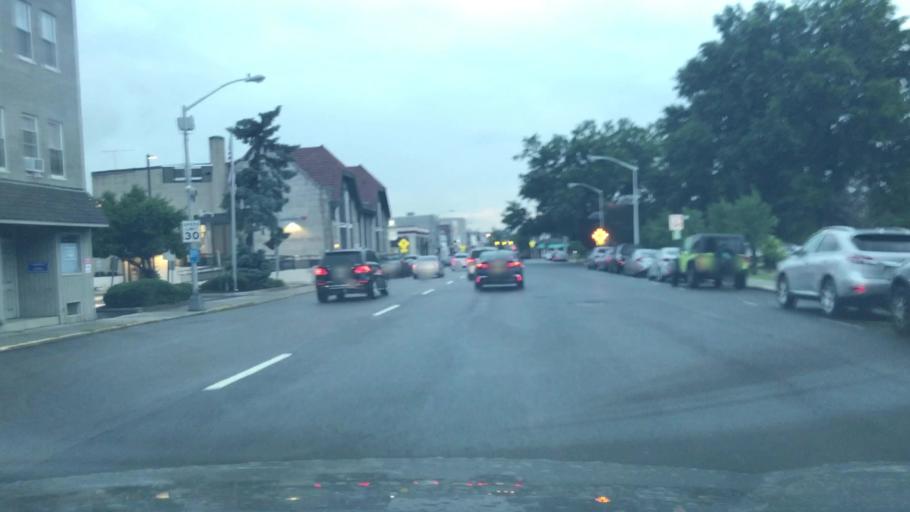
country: US
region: New Jersey
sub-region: Bergen County
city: Englewood
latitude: 40.8969
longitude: -73.9725
